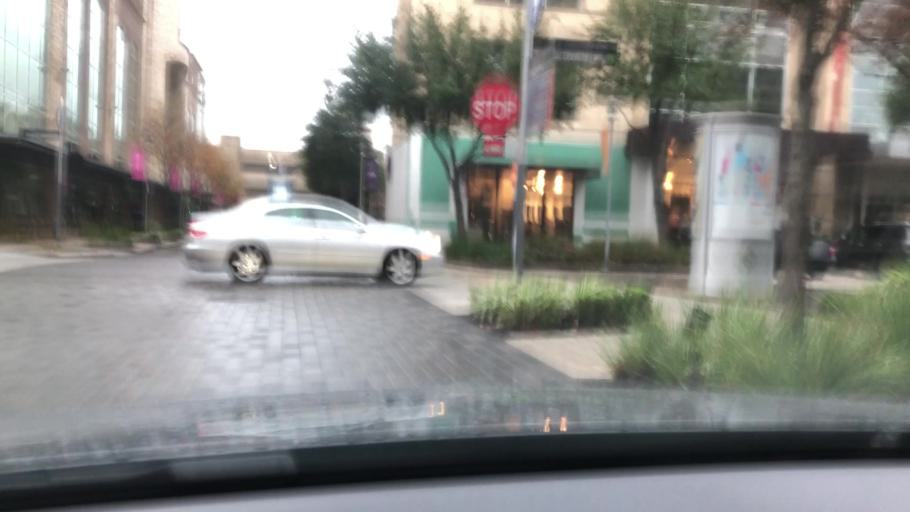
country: US
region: Texas
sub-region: Harris County
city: Bunker Hill Village
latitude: 29.7806
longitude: -95.5609
